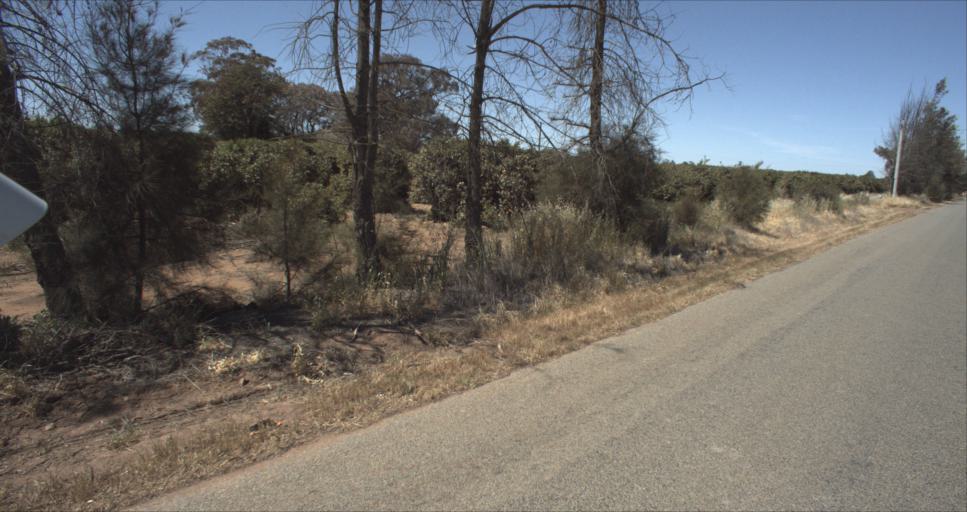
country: AU
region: New South Wales
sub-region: Leeton
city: Leeton
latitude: -34.5349
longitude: 146.3565
